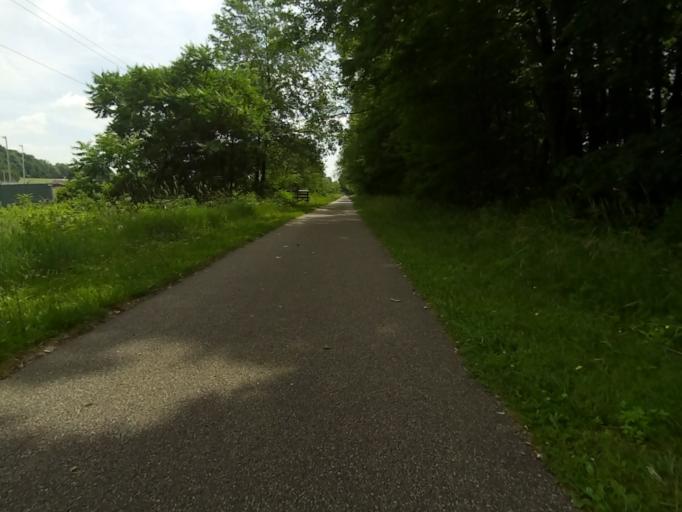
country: US
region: Ohio
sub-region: Summit County
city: Stow
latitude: 41.1926
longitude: -81.4116
